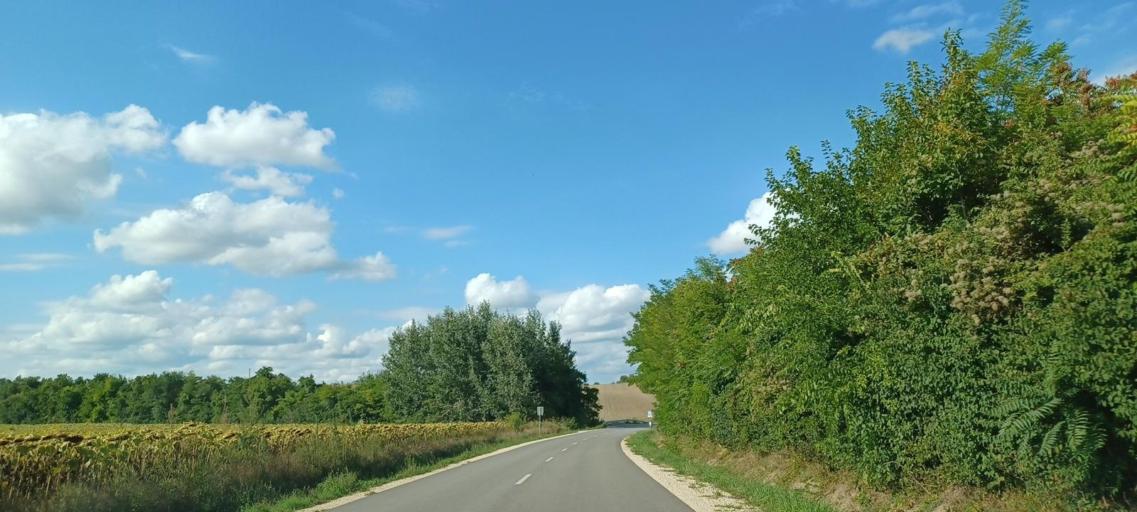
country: HU
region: Tolna
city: Zomba
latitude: 46.4795
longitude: 18.5948
